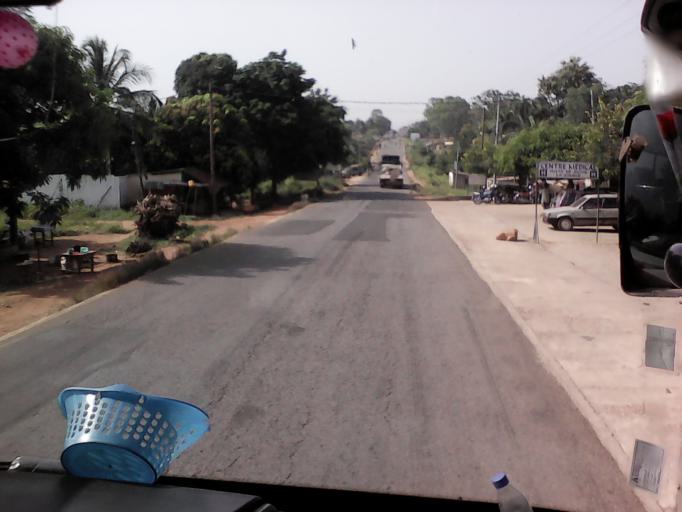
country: TG
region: Centrale
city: Sokode
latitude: 9.0144
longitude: 1.1383
